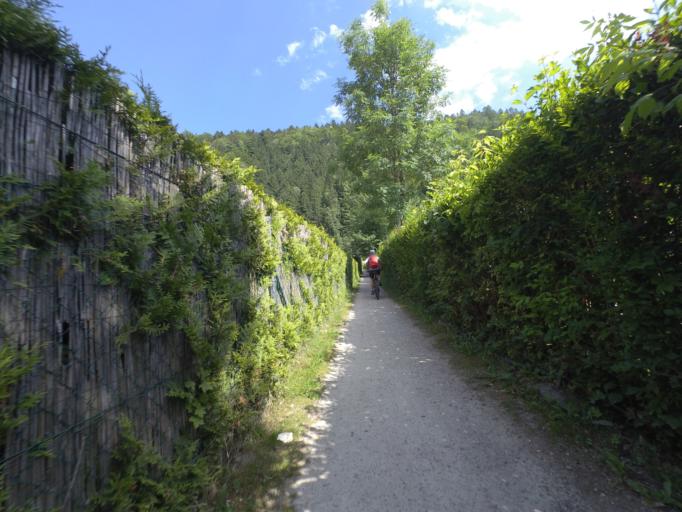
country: AT
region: Carinthia
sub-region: Politischer Bezirk Villach Land
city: Ferndorf
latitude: 46.7685
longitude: 13.6480
